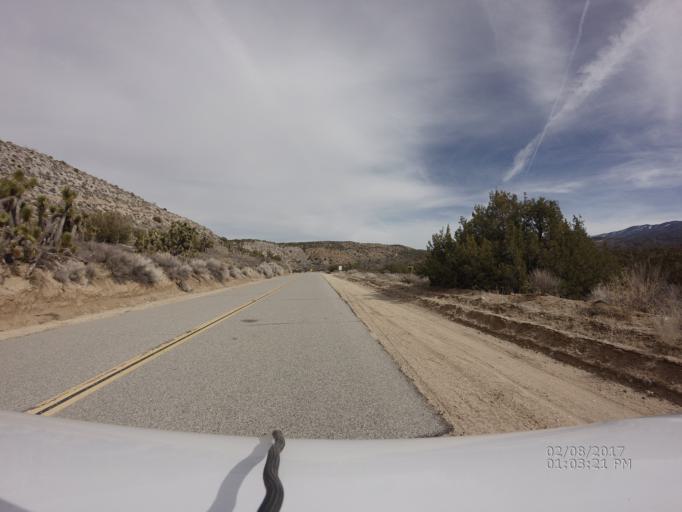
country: US
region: California
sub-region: Los Angeles County
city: Lake Los Angeles
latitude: 34.4504
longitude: -117.8167
